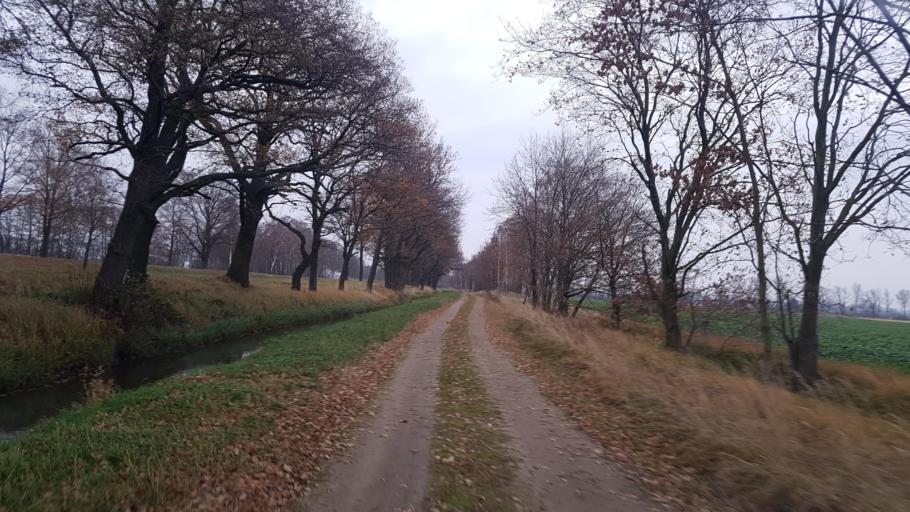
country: DE
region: Brandenburg
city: Hirschfeld
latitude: 51.4130
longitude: 13.6146
